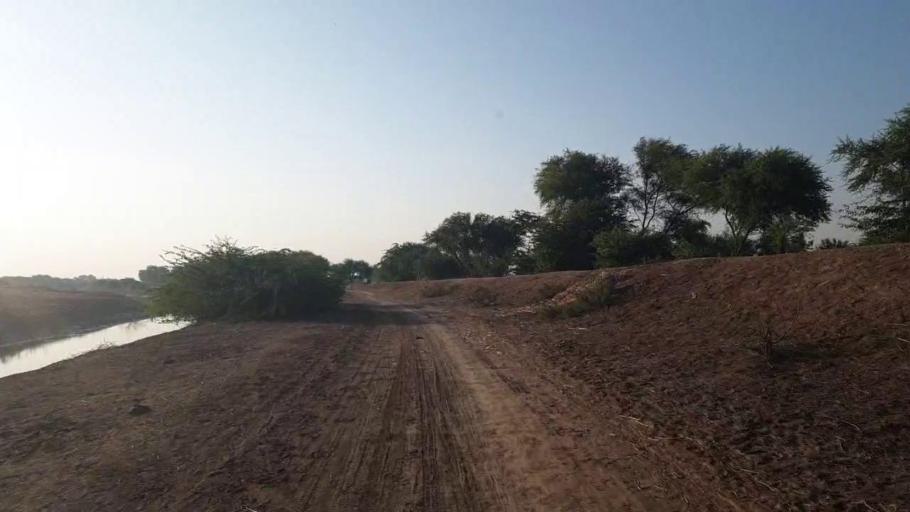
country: PK
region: Sindh
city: Badin
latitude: 24.6382
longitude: 68.7919
